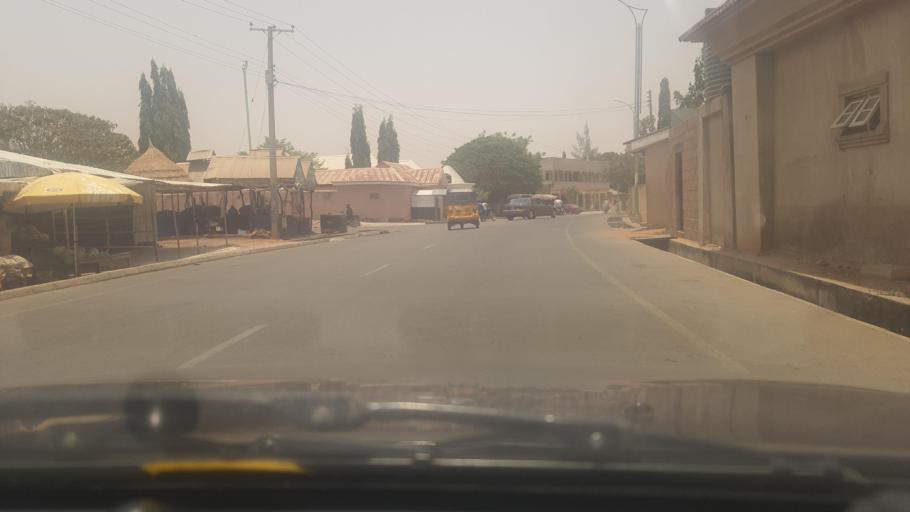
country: NG
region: Gombe
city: Gombe
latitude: 10.2968
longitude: 11.1540
